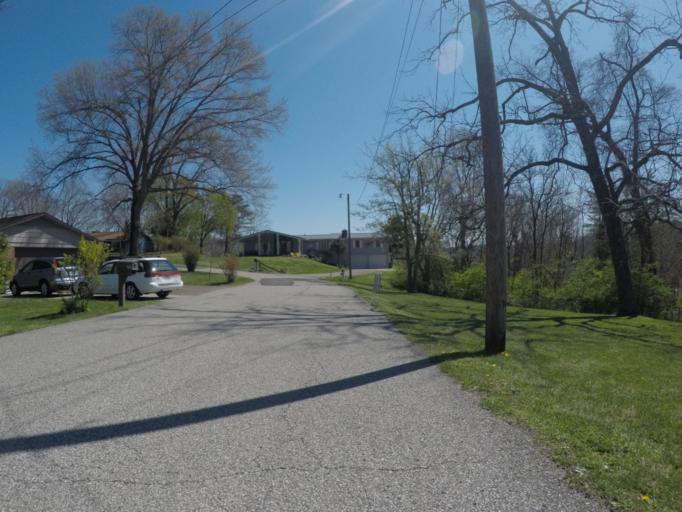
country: US
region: West Virginia
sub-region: Cabell County
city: Pea Ridge
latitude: 38.4134
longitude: -82.3188
